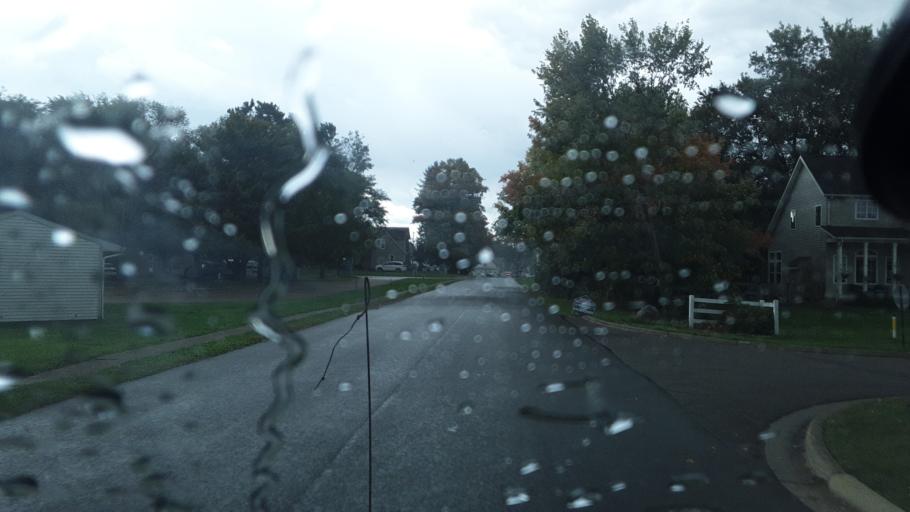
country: US
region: Ohio
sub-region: Knox County
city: Centerburg
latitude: 40.3085
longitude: -82.6980
